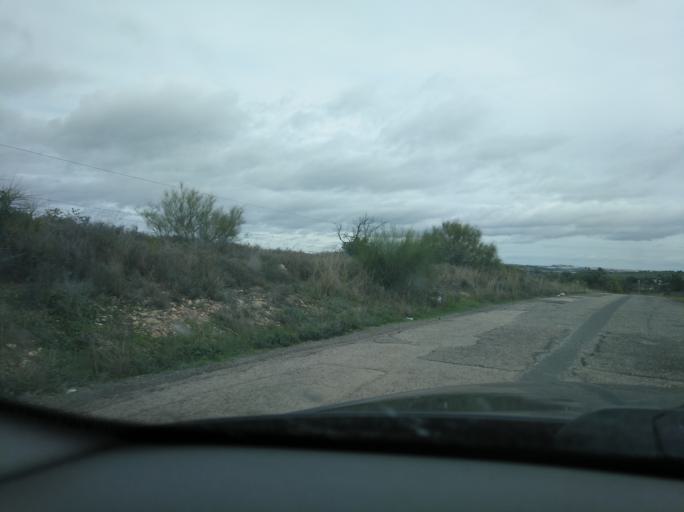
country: PT
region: Faro
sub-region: Vila Real de Santo Antonio
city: Monte Gordo
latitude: 37.1963
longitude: -7.4944
